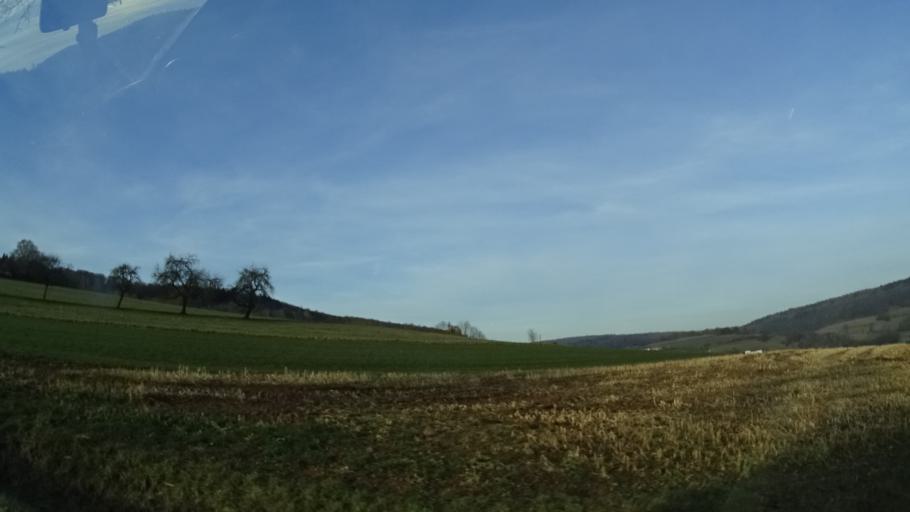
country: DE
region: Bavaria
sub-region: Regierungsbezirk Unterfranken
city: Bad Bruckenau
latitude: 50.3083
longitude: 9.7255
